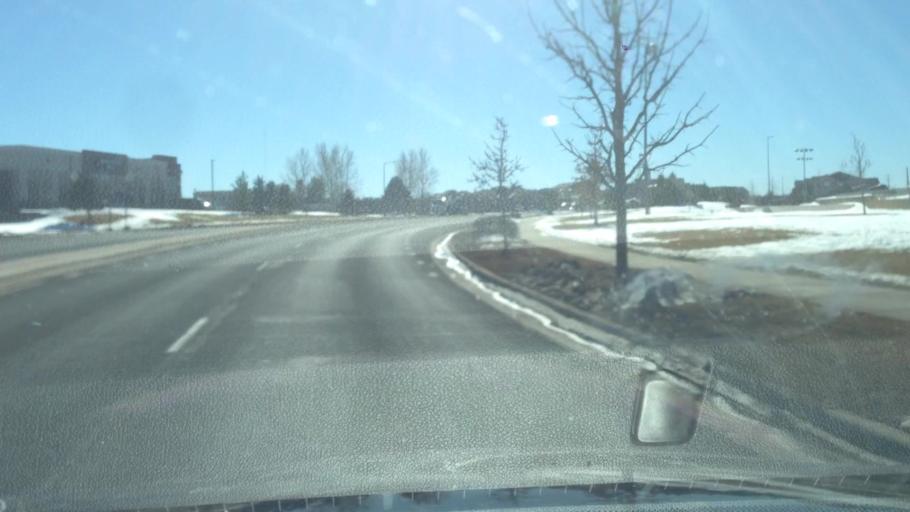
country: US
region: Colorado
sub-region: Douglas County
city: Parker
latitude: 39.5260
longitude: -104.7771
